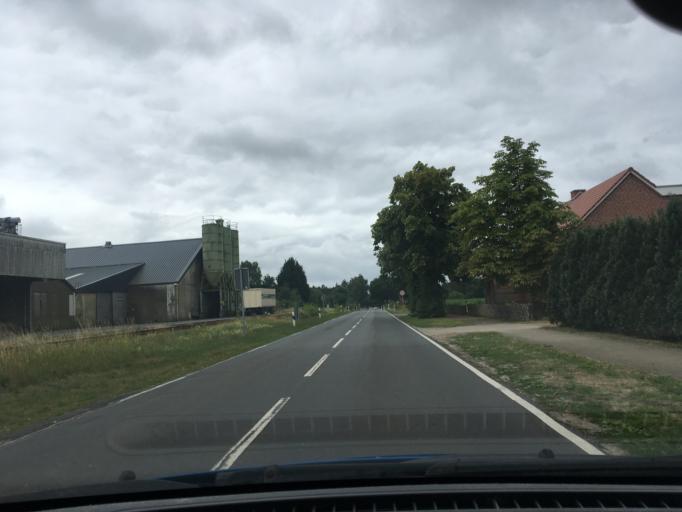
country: DE
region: Lower Saxony
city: Wulfsen
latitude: 53.2931
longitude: 10.1453
